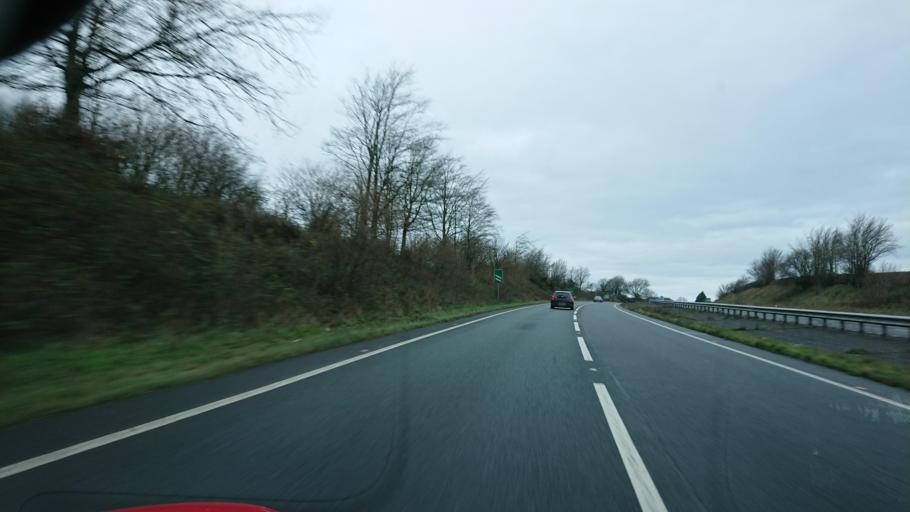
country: GB
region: England
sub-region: Cornwall
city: Liskeard
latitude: 50.4310
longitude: -4.4349
